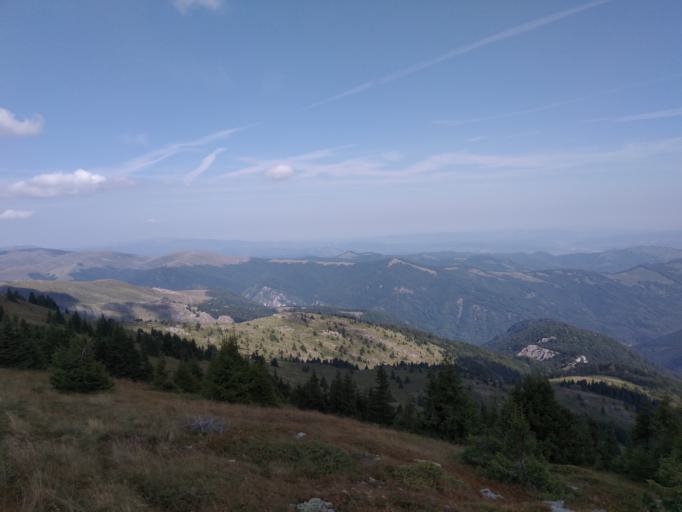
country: BG
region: Plovdiv
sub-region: Obshtina Karlovo
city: Karlovo
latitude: 42.7293
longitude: 24.7524
